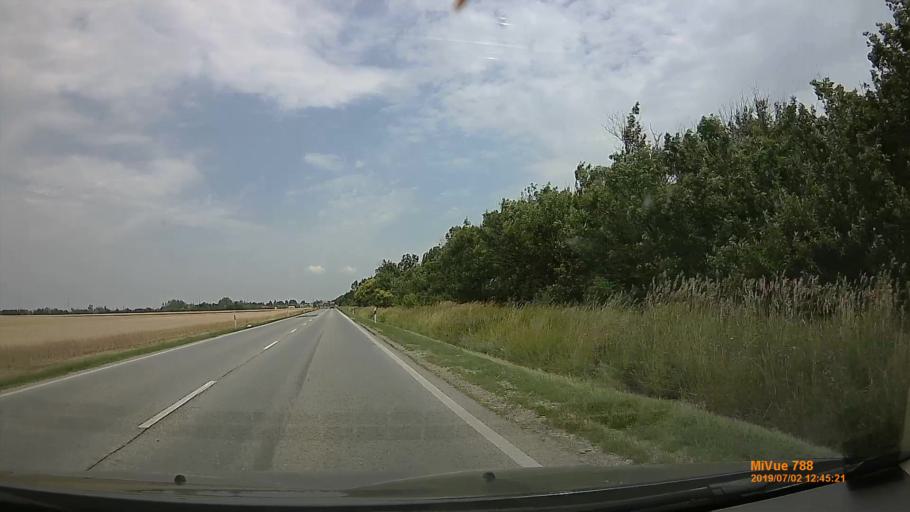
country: HU
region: Gyor-Moson-Sopron
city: Mosonmagyarovar
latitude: 47.8342
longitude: 17.2167
